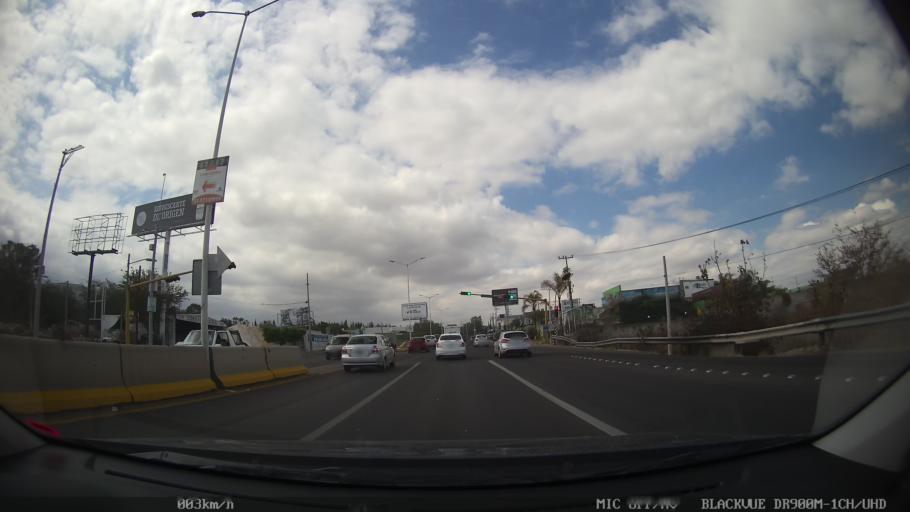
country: MX
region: Jalisco
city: Tonala
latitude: 20.6356
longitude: -103.2437
